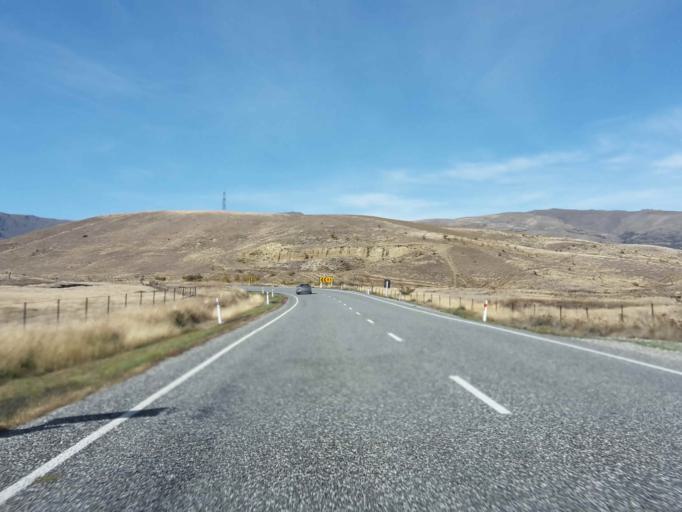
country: NZ
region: Otago
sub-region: Queenstown-Lakes District
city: Wanaka
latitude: -44.8080
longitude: 169.4875
